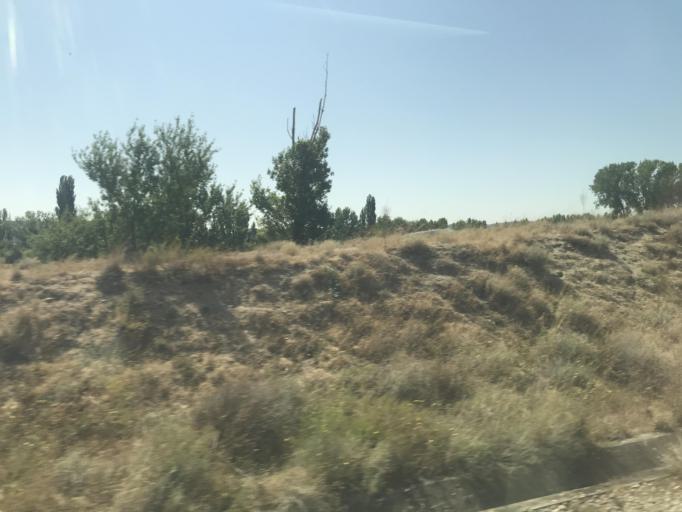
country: ES
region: Castille and Leon
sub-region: Provincia de Palencia
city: Soto de Cerrato
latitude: 41.9520
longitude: -4.4538
